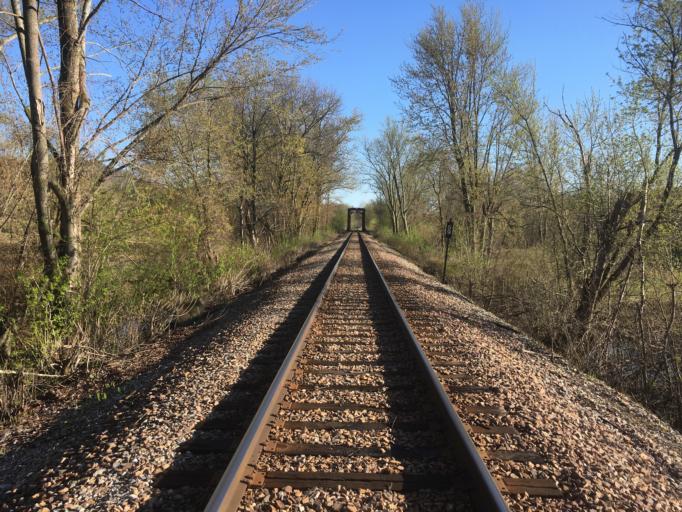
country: US
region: Vermont
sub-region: Rutland County
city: West Rutland
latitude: 43.6405
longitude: -73.0361
